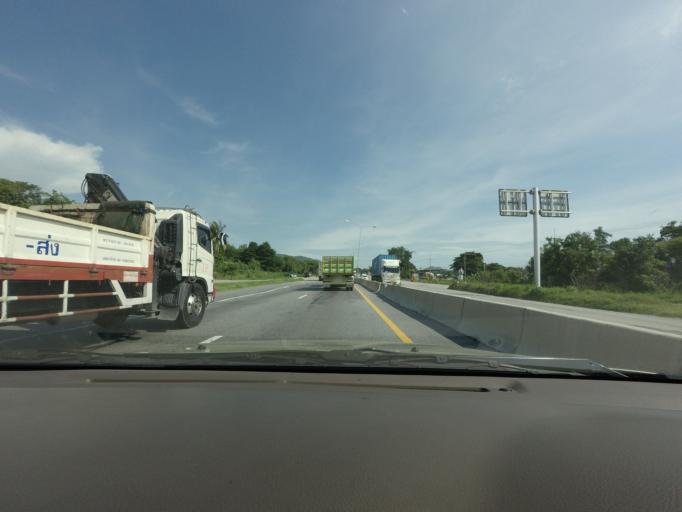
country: TH
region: Chon Buri
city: Chon Buri
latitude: 13.3281
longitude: 100.9899
